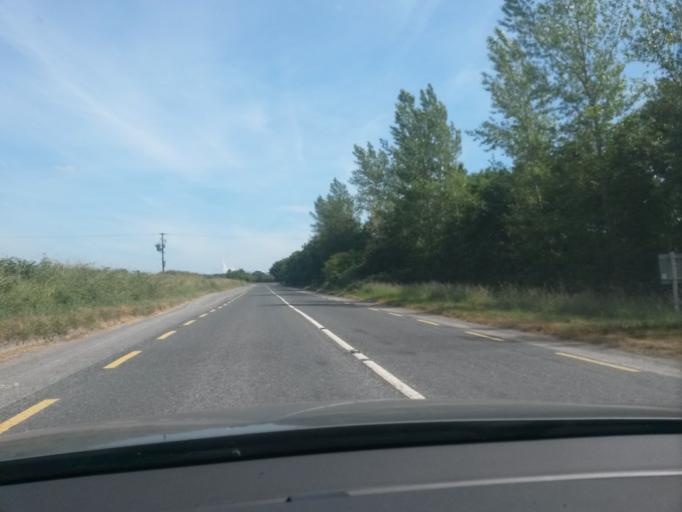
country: IE
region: Leinster
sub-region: Kildare
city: Naas
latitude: 53.2085
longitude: -6.6387
